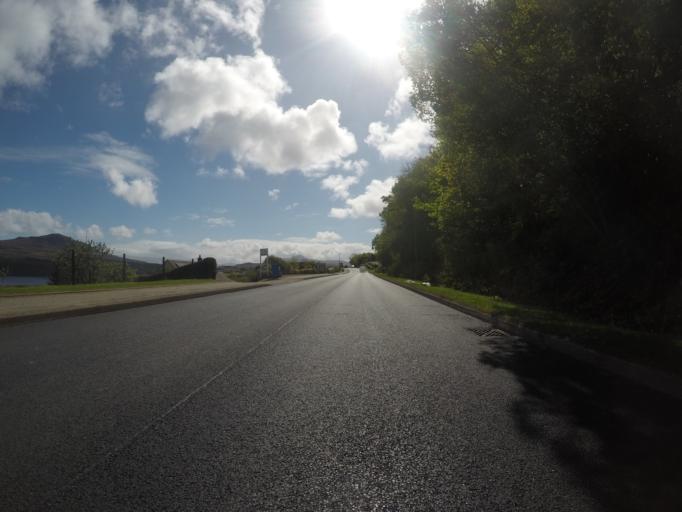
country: GB
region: Scotland
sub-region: Highland
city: Portree
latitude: 57.4072
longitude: -6.2014
